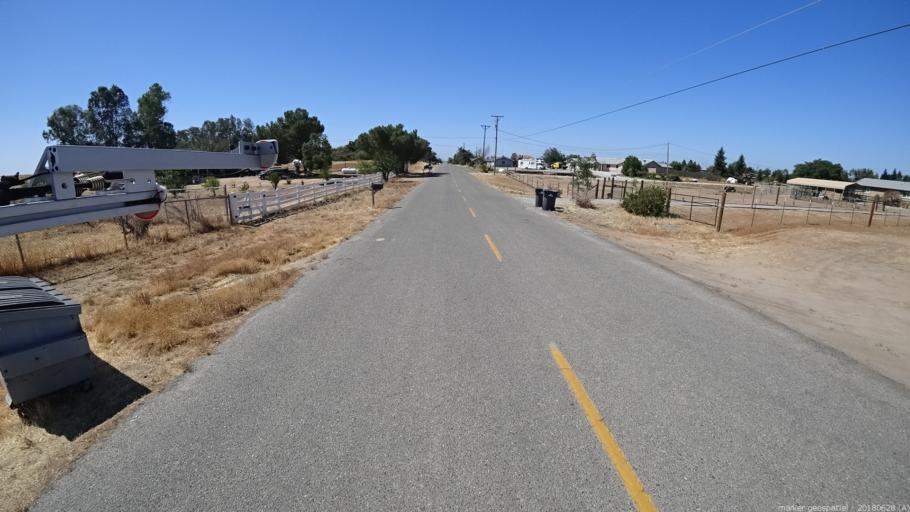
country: US
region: California
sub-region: Madera County
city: Bonadelle Ranchos-Madera Ranchos
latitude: 36.9925
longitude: -119.8685
